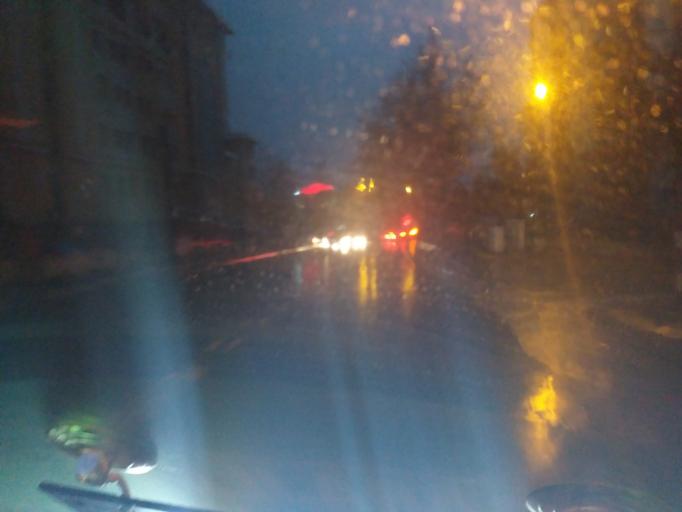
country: TR
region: Ankara
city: Ankara
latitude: 39.9430
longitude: 32.8249
